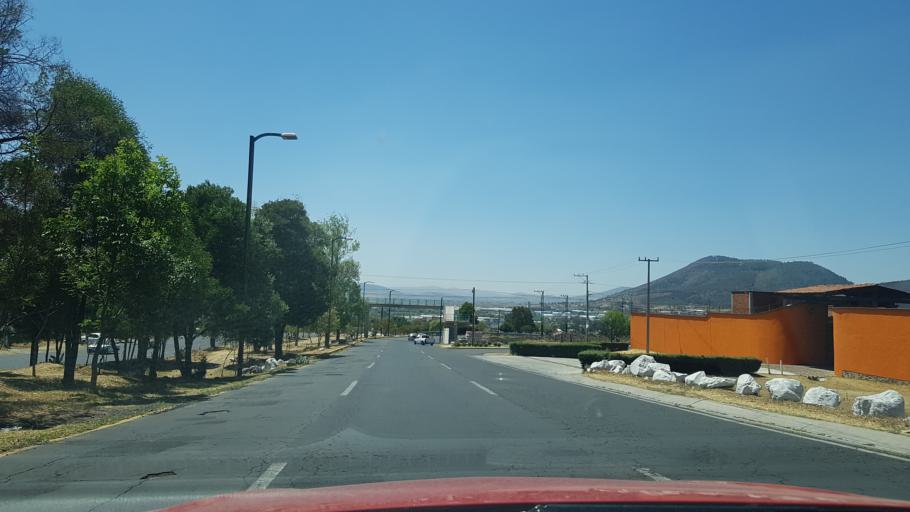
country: MX
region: Mexico
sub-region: Atlacomulco
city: Santa Cruz Bombatevi
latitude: 19.8044
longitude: -99.8804
